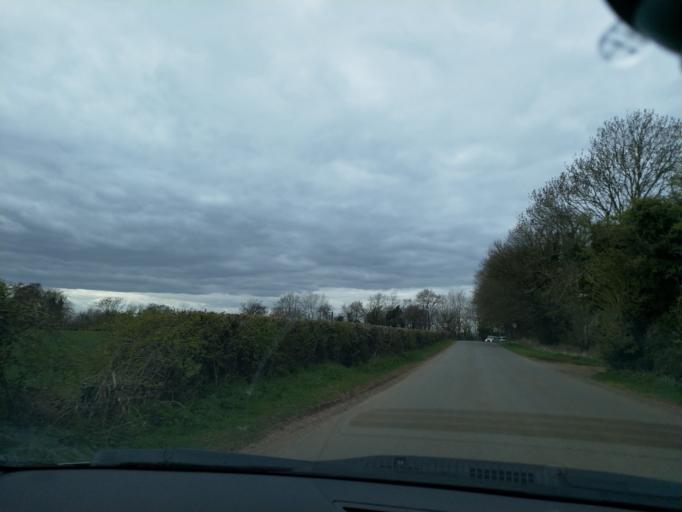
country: GB
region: England
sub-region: Oxfordshire
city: Hanwell
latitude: 52.1259
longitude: -1.4472
